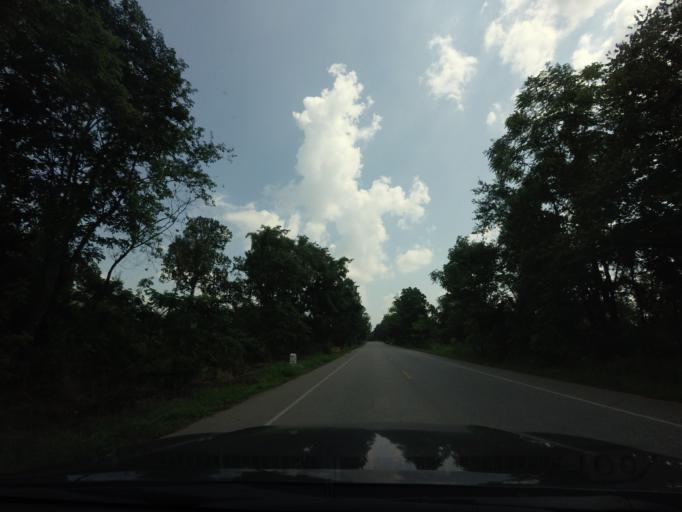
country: TH
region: Phitsanulok
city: Chat Trakan
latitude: 17.2750
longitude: 100.5415
